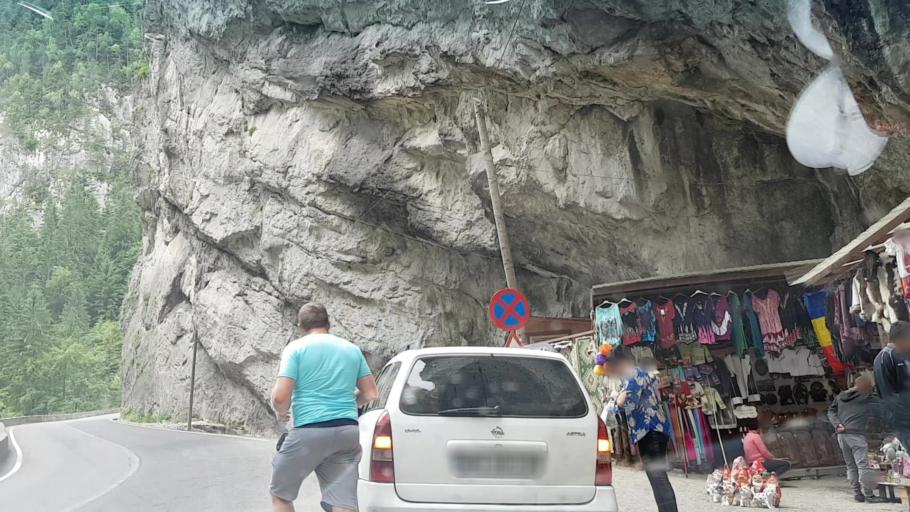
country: RO
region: Neamt
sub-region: Comuna Bicaz Chei
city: Bicaz Chei
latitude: 46.8118
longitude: 25.8286
